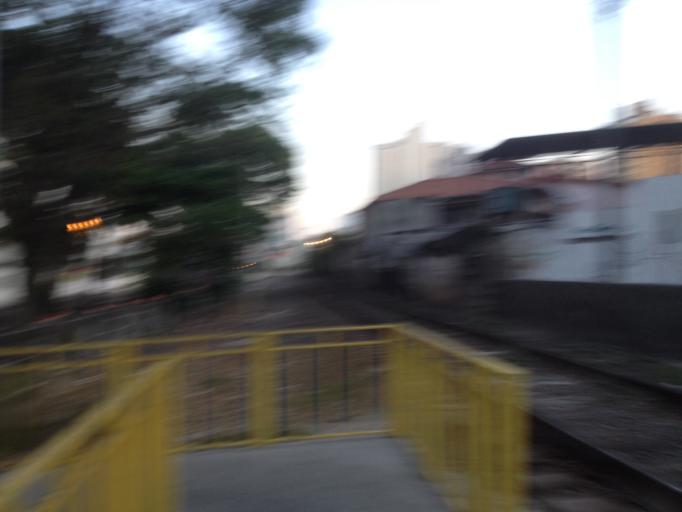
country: BR
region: Minas Gerais
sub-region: Juiz De Fora
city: Juiz de Fora
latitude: -21.7507
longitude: -43.3528
